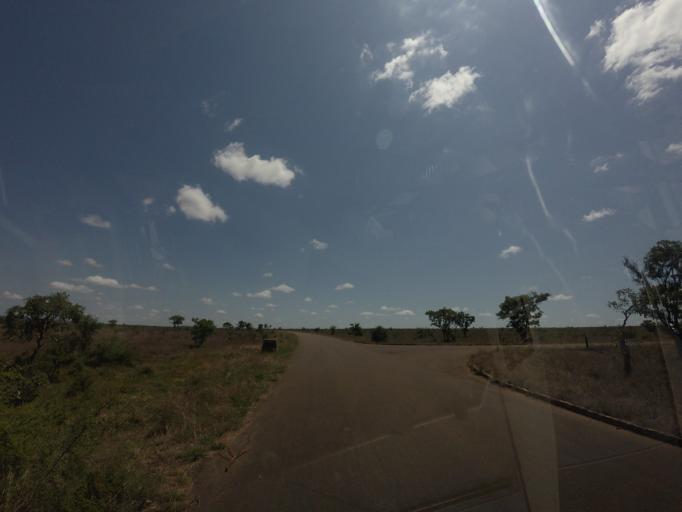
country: ZA
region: Mpumalanga
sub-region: Ehlanzeni District
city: Komatipoort
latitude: -24.9553
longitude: 31.9216
